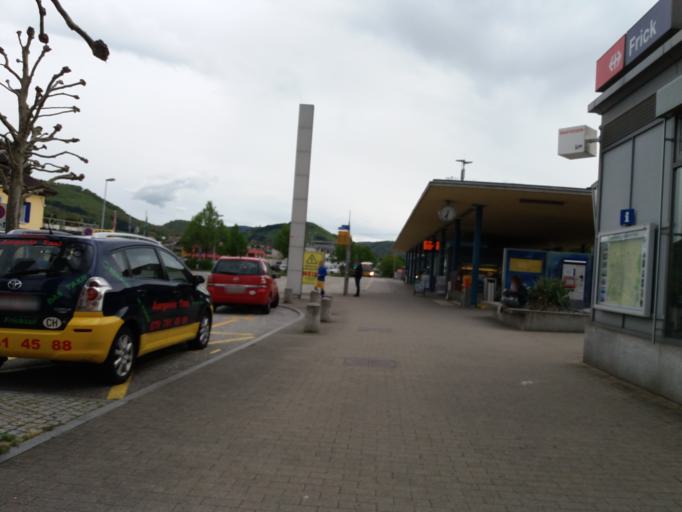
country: CH
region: Aargau
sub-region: Bezirk Laufenburg
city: Gipf-Oberfrick
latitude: 47.5073
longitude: 8.0133
